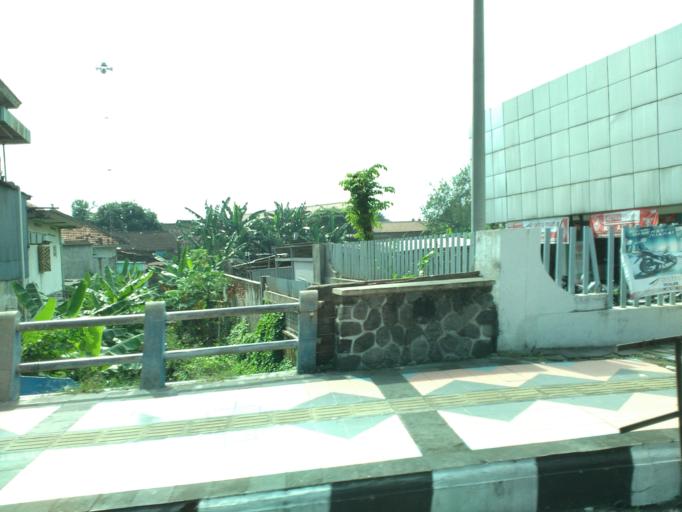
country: ID
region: Central Java
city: Klaten
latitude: -7.7001
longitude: 110.6051
